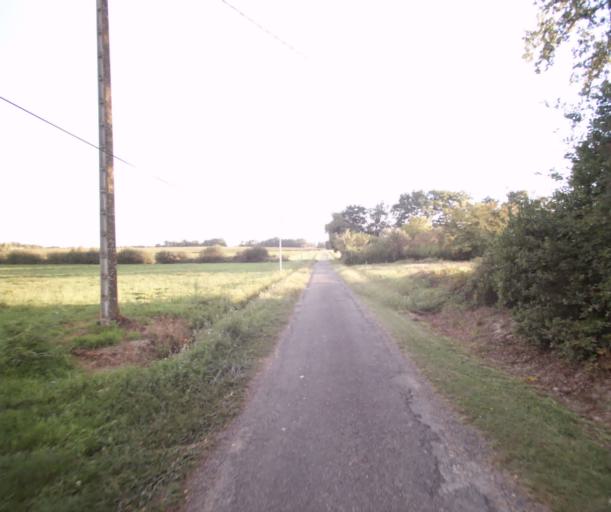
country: FR
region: Midi-Pyrenees
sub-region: Departement du Gers
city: Eauze
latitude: 43.8870
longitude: 0.0705
